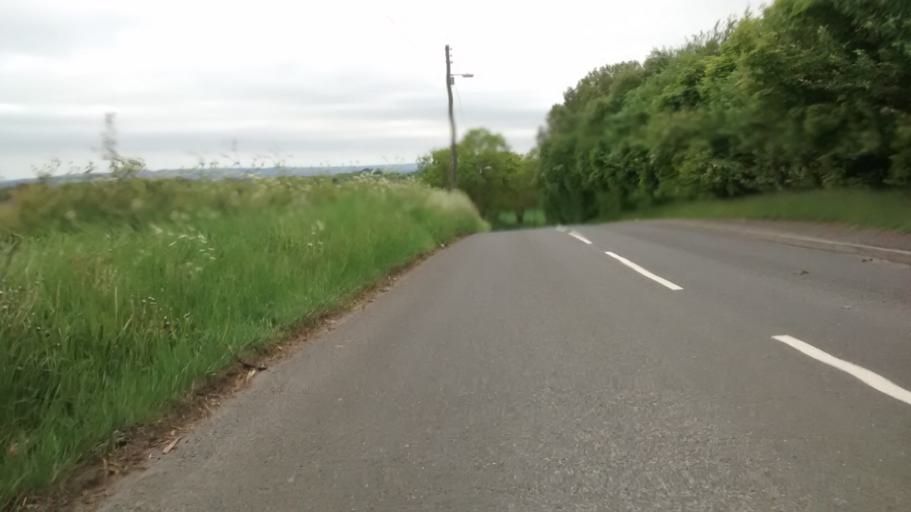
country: GB
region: England
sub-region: County Durham
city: Pittington
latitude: 54.7855
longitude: -1.4768
